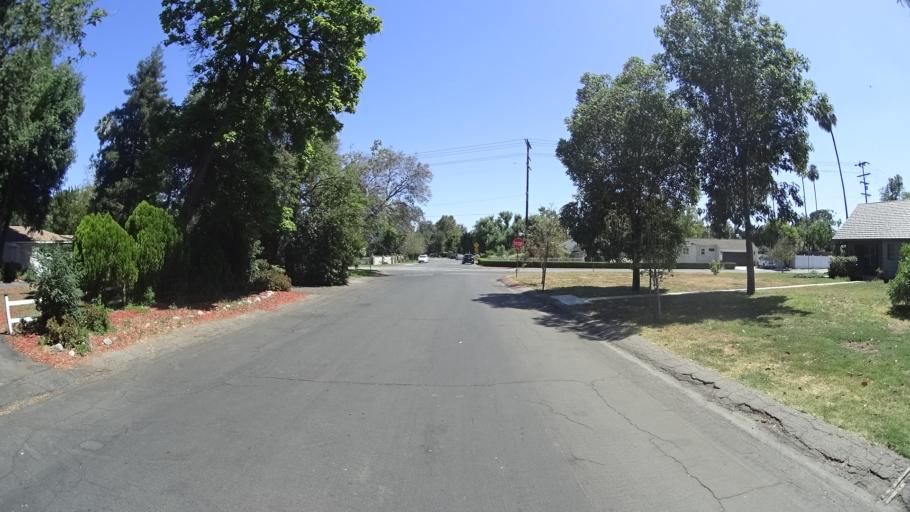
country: US
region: California
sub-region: Los Angeles County
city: Van Nuys
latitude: 34.1895
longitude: -118.4692
